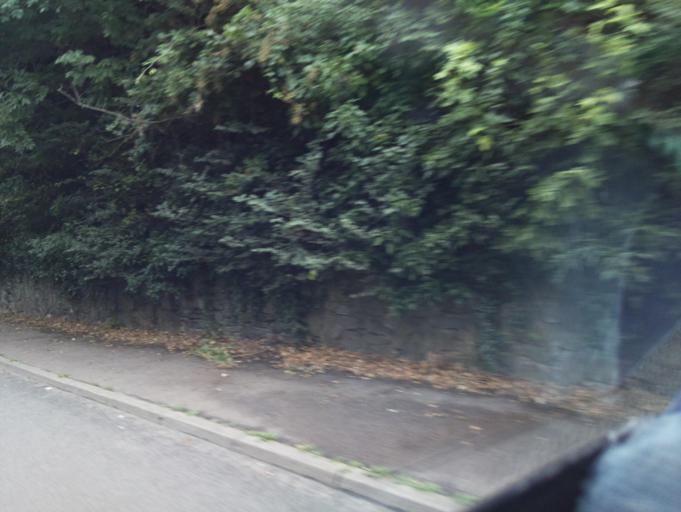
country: GB
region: England
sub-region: Worcestershire
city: Droitwich
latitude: 52.2532
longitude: -2.1605
